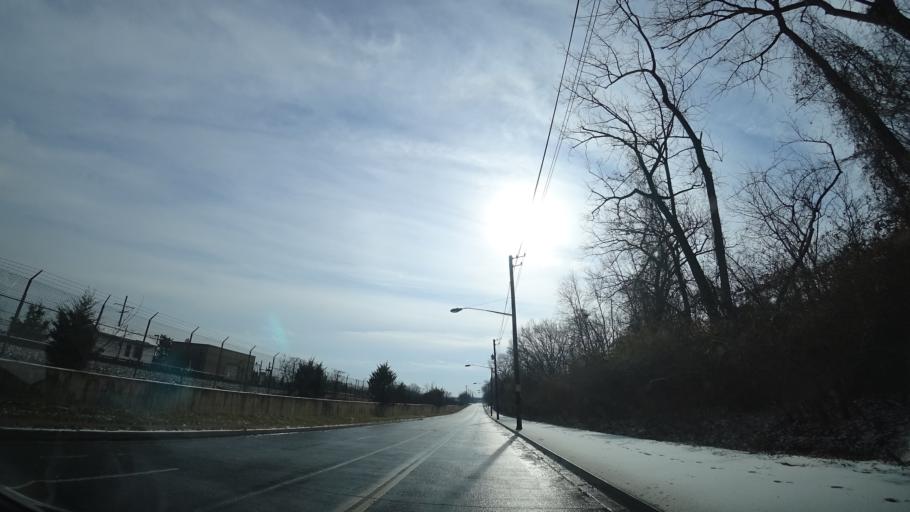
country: US
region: Maryland
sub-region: Prince George's County
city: Chillum
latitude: 38.9464
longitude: -77.0002
